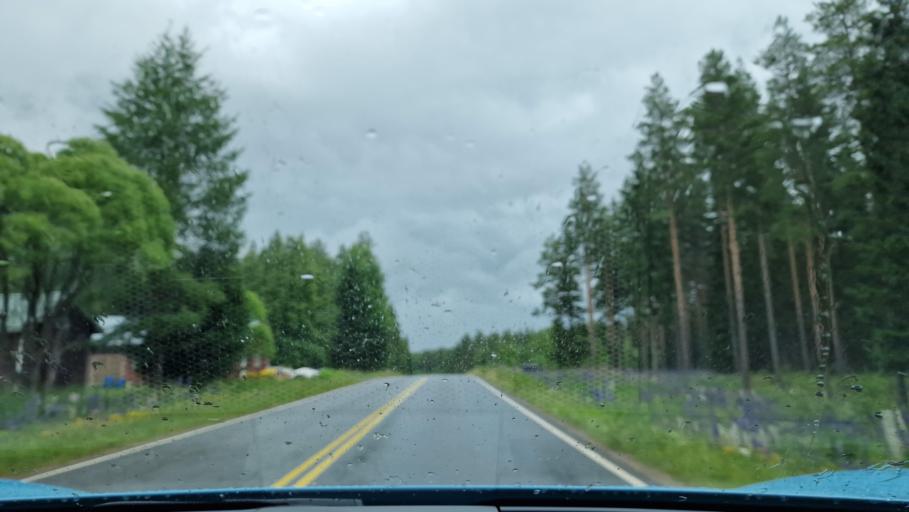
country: FI
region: Southern Ostrobothnia
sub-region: Jaerviseutu
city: Soini
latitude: 62.7954
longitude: 24.3748
